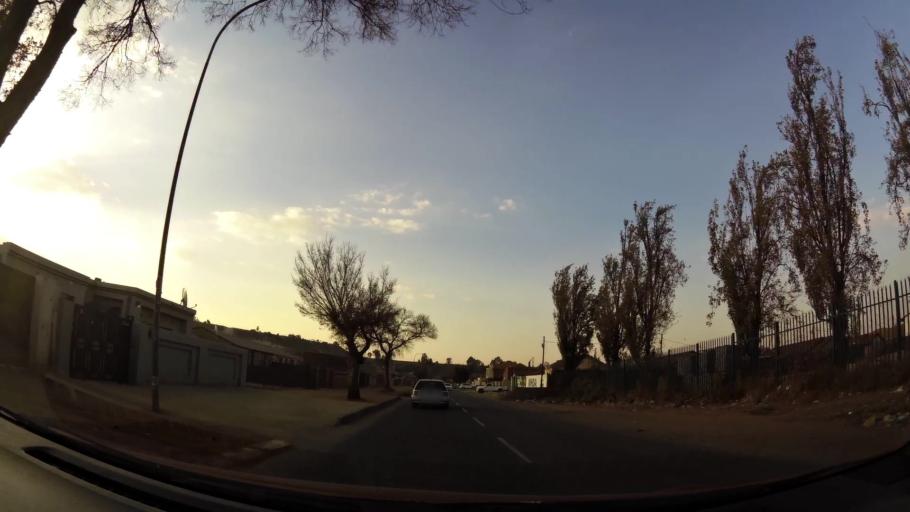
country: ZA
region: Gauteng
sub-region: City of Johannesburg Metropolitan Municipality
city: Roodepoort
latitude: -26.2114
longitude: 27.8950
